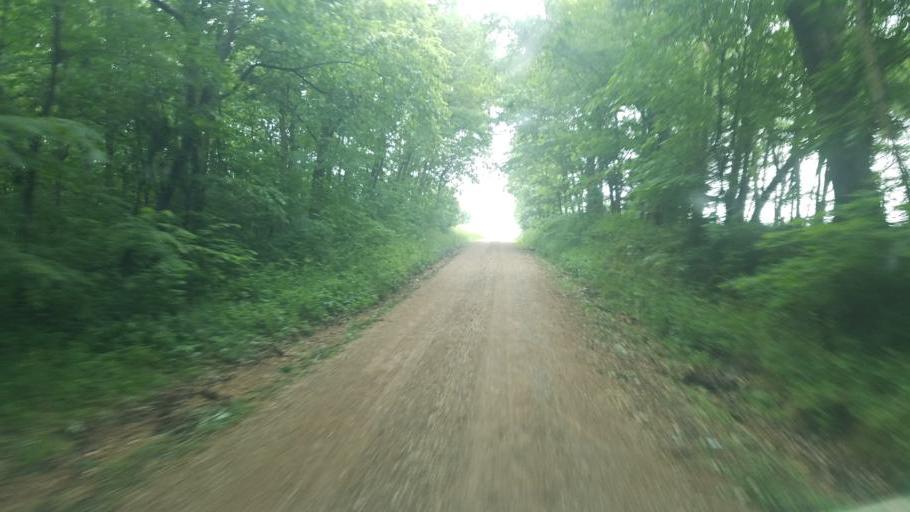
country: US
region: Missouri
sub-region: Moniteau County
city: California
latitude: 38.5927
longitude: -92.6495
